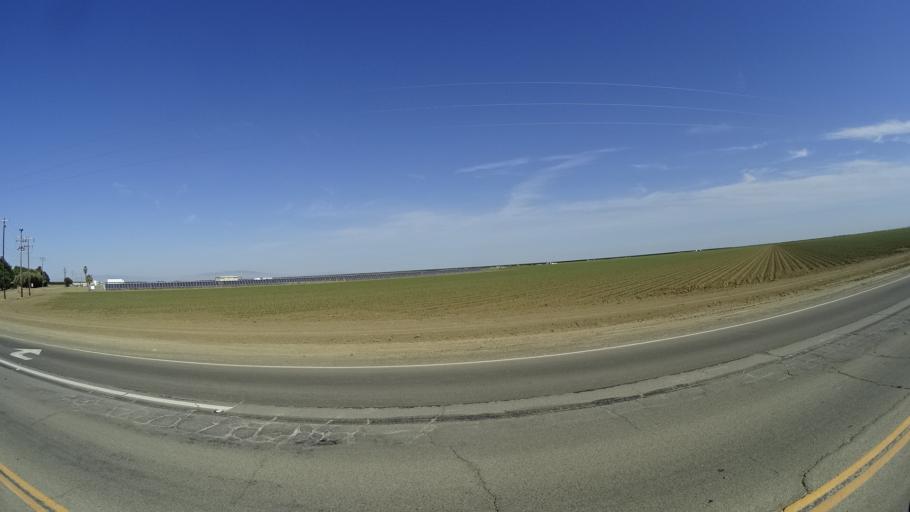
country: US
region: California
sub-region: Kings County
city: Lemoore Station
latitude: 36.1817
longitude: -119.9552
